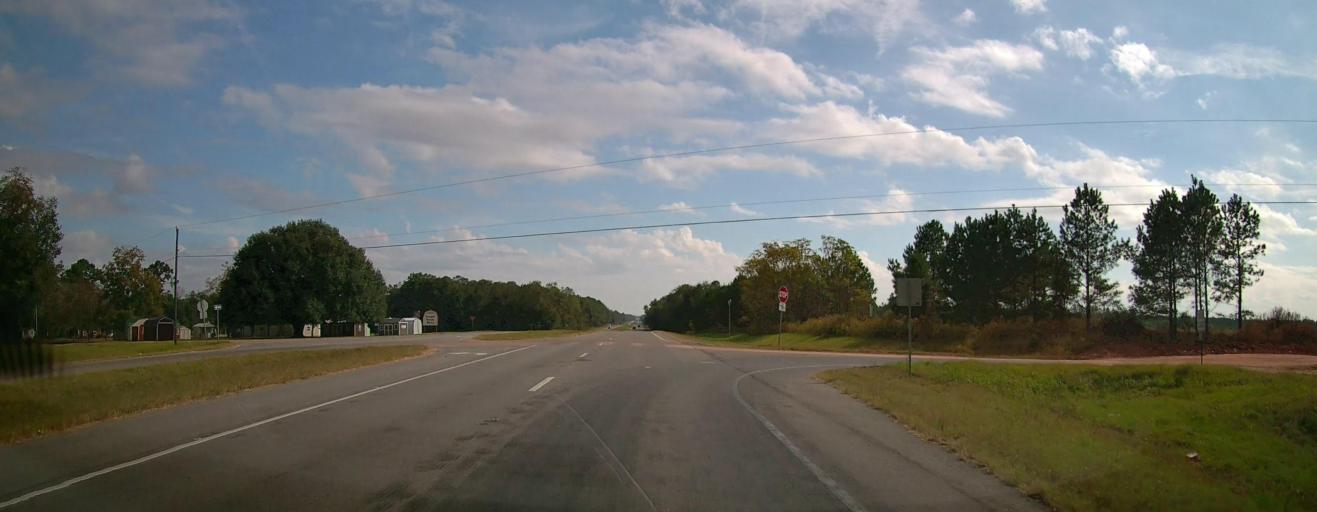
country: US
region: Georgia
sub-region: Thomas County
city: Meigs
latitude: 31.0099
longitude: -84.0527
